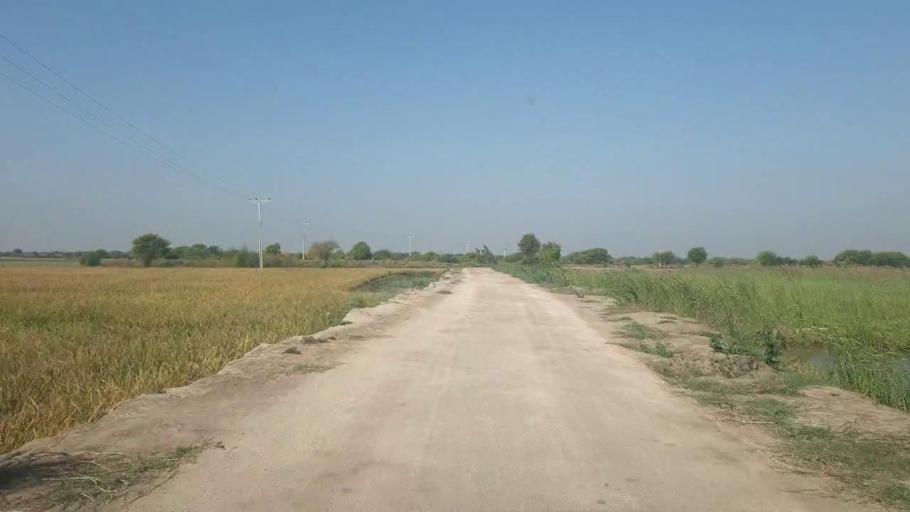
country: PK
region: Sindh
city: Tando Bago
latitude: 24.7358
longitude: 68.8901
